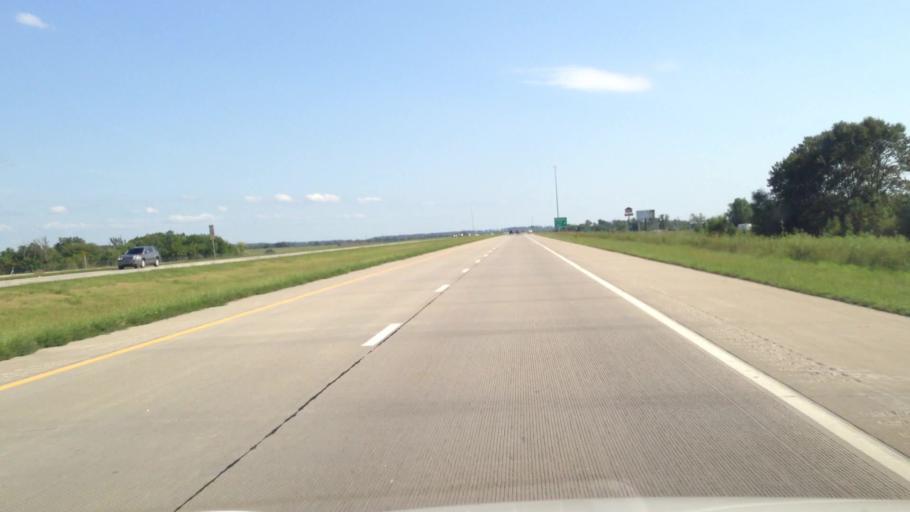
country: US
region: Kansas
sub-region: Linn County
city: Pleasanton
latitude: 38.1888
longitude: -94.7037
